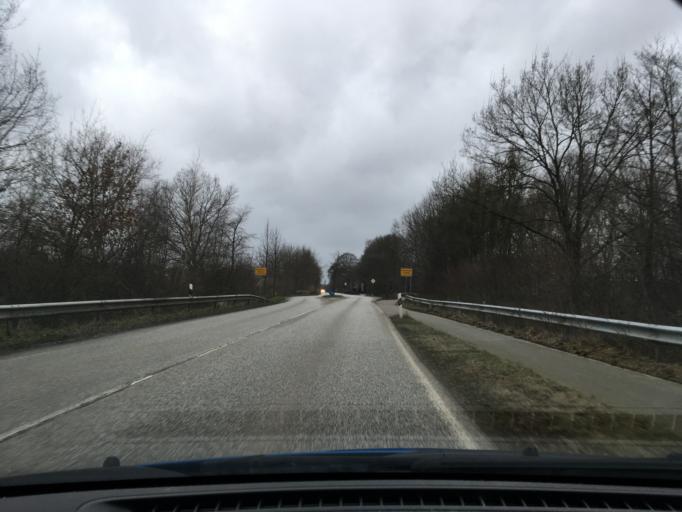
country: DE
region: Schleswig-Holstein
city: Grabau
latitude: 53.4965
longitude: 10.5052
